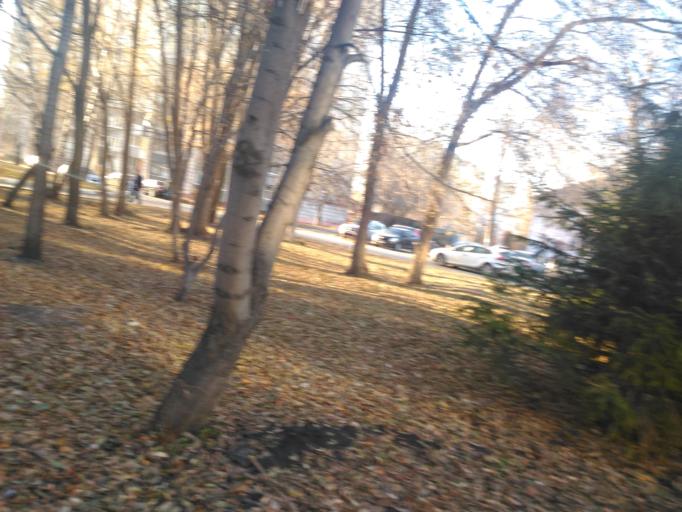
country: RU
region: Ulyanovsk
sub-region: Ulyanovskiy Rayon
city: Ulyanovsk
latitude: 54.3238
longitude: 48.3824
